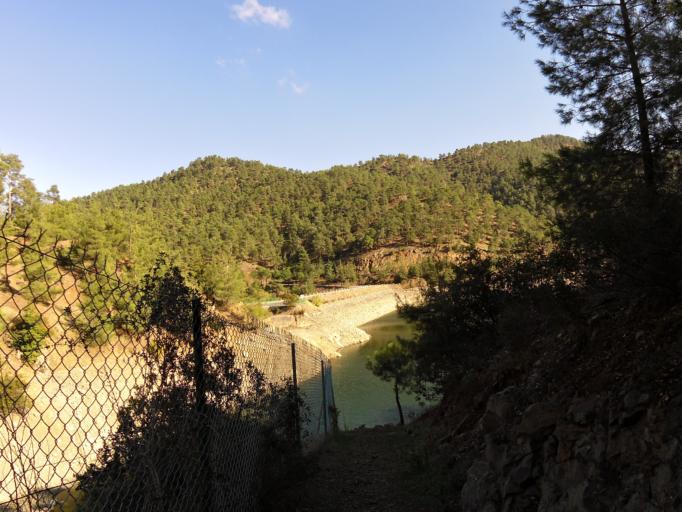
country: CY
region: Limassol
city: Kyperounta
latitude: 35.0091
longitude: 33.0350
